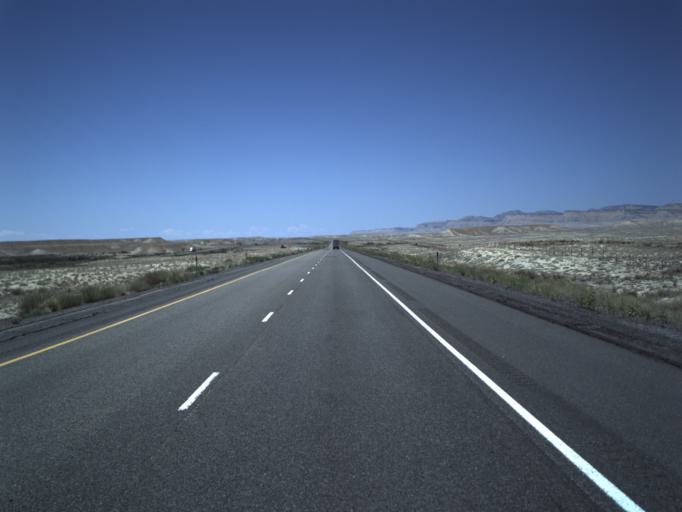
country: US
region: Utah
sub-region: Grand County
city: Moab
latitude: 38.9394
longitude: -109.4967
